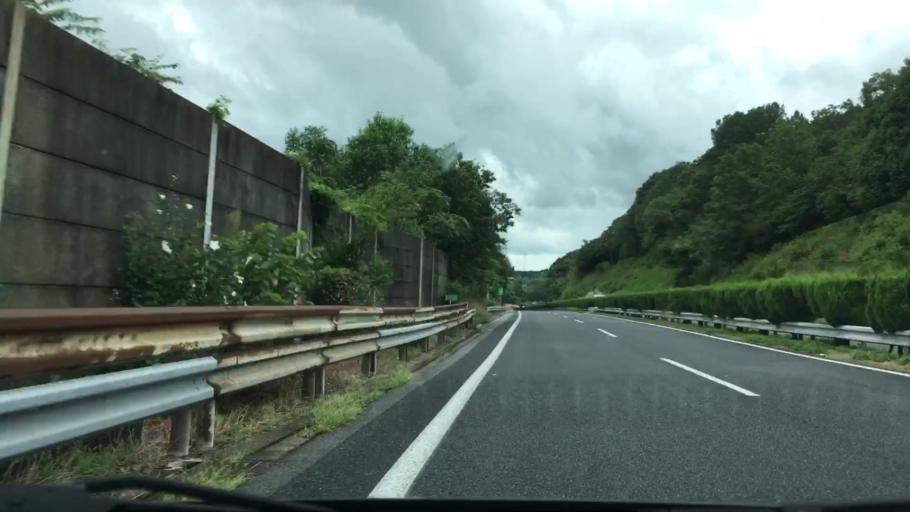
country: JP
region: Okayama
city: Tsuyama
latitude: 35.0418
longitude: 134.1231
